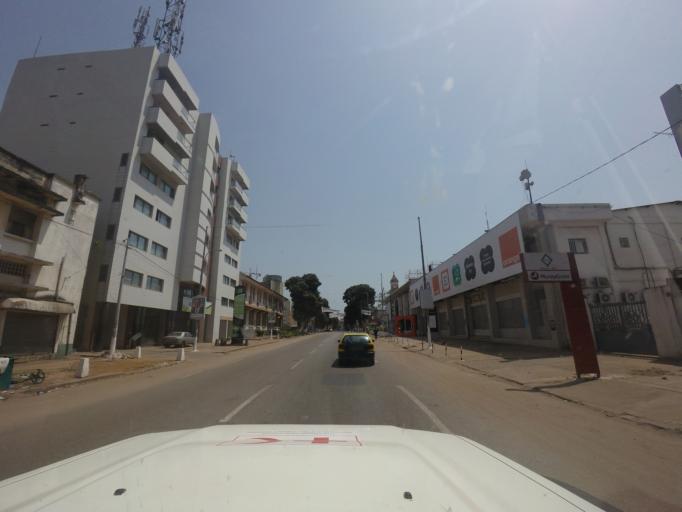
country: GN
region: Conakry
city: Camayenne
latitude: 9.5121
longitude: -13.7145
